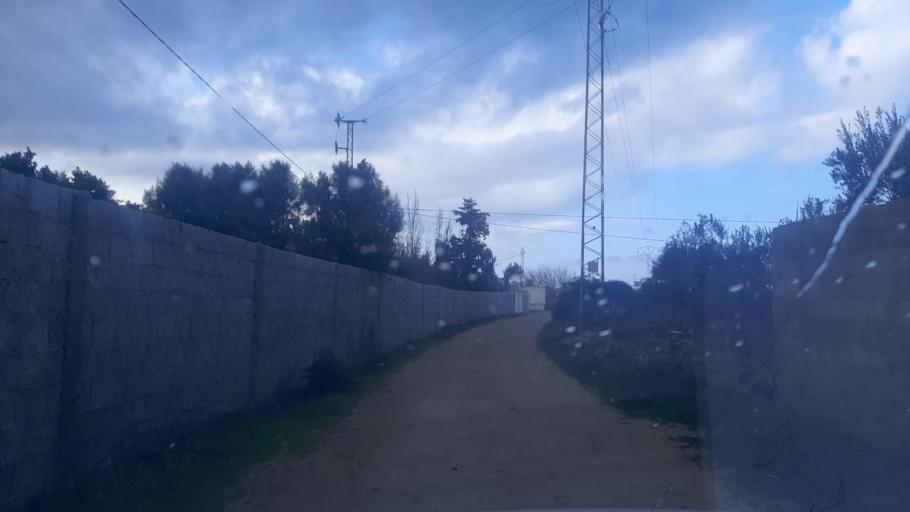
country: TN
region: Nabul
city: Manzil Bu Zalafah
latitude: 36.7422
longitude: 10.5277
